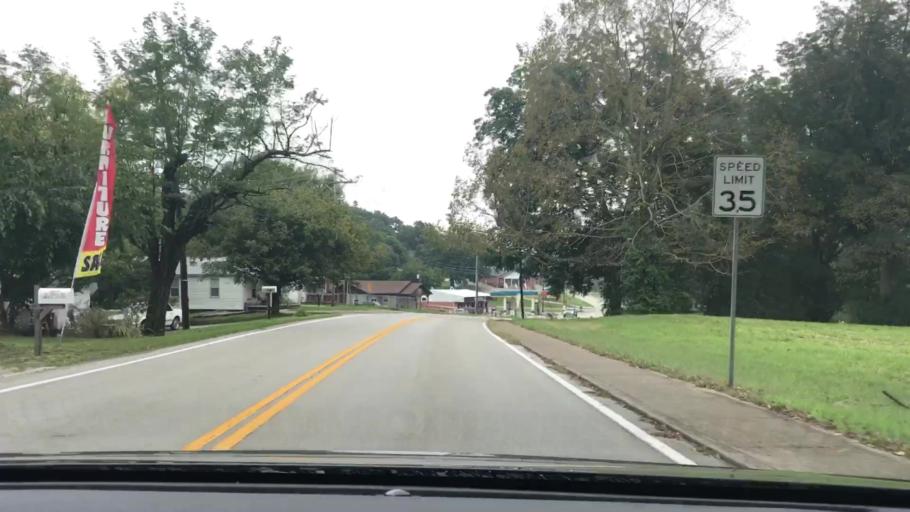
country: US
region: Kentucky
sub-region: Pulaski County
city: Somerset
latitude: 37.0899
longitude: -84.5909
